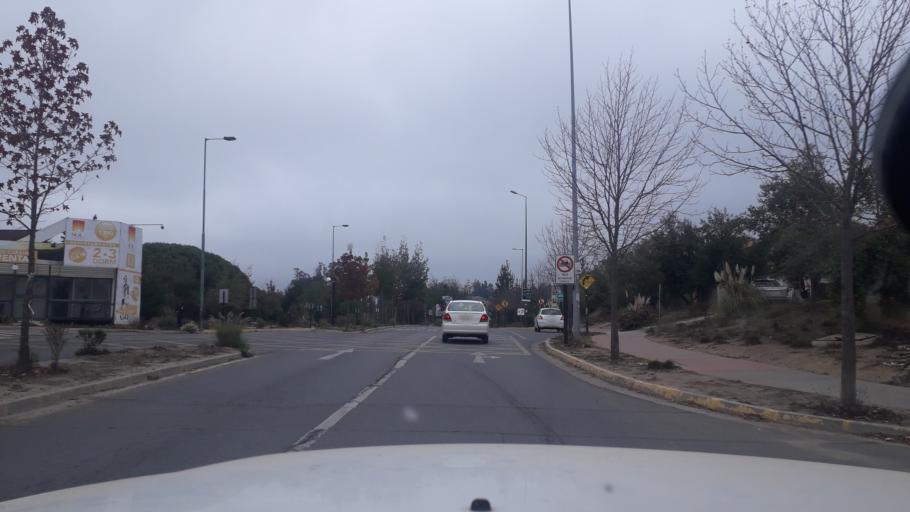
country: CL
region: Valparaiso
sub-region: Provincia de Valparaiso
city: Vina del Mar
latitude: -33.1337
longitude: -71.5684
